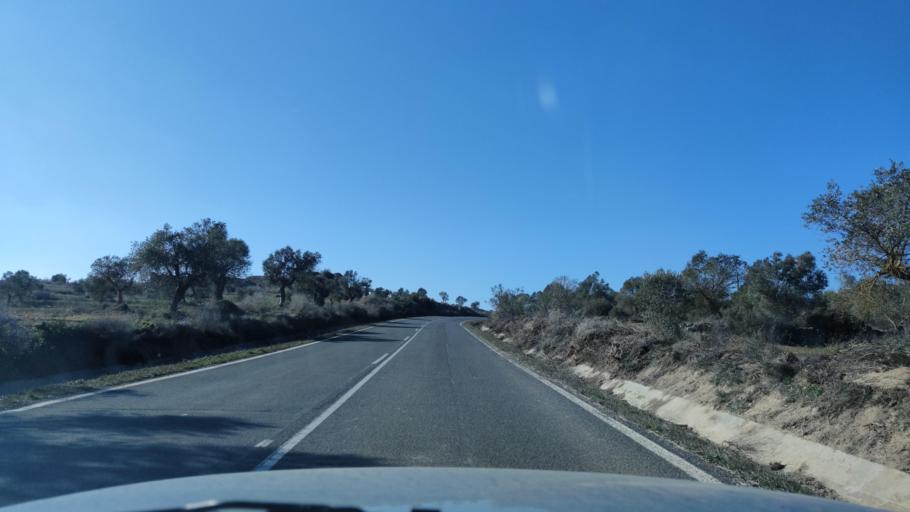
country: ES
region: Catalonia
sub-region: Provincia de Lleida
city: Maials
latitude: 41.3334
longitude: 0.4464
